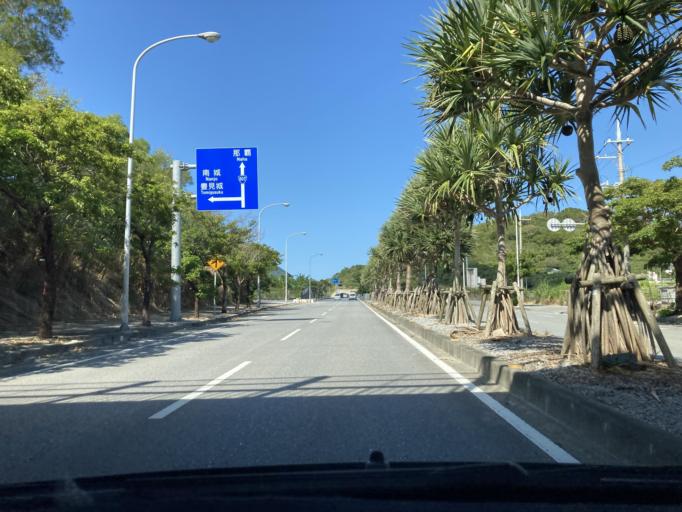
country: JP
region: Okinawa
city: Tomigusuku
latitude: 26.1838
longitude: 127.7223
